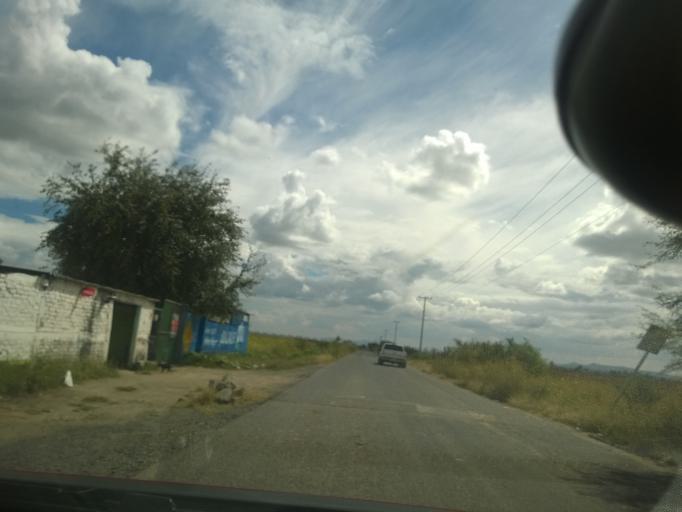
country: MX
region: Guanajuato
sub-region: Leon
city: El CERESO
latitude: 20.9749
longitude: -101.6530
